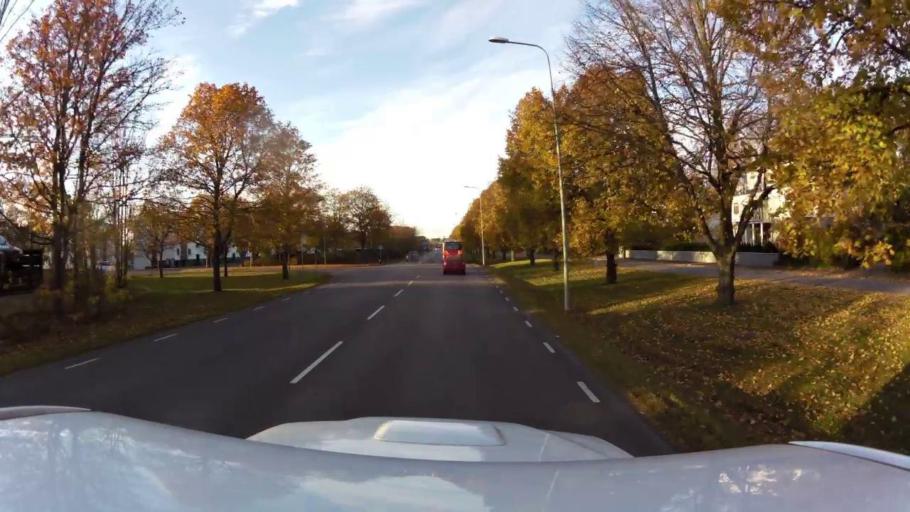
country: SE
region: OEstergoetland
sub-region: Linkopings Kommun
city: Linkoping
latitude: 58.3906
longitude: 15.6486
